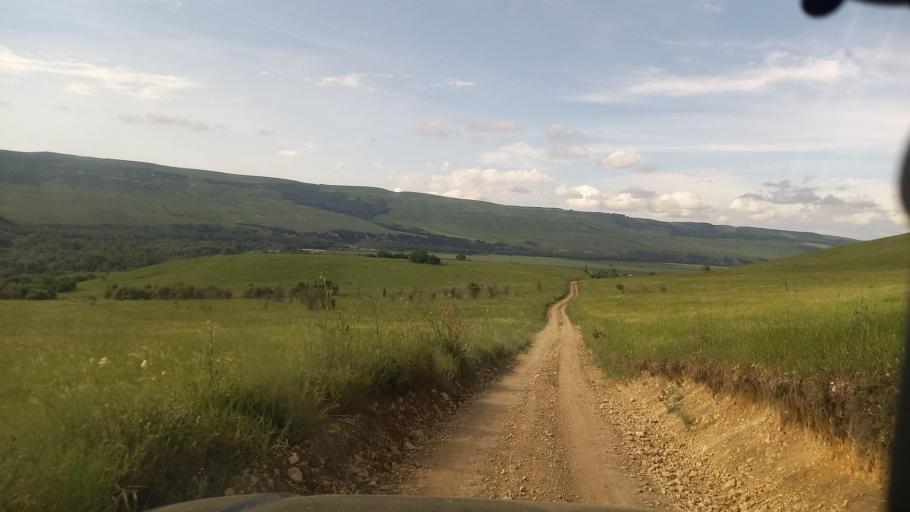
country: RU
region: Krasnodarskiy
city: Peredovaya
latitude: 44.0769
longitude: 41.3637
